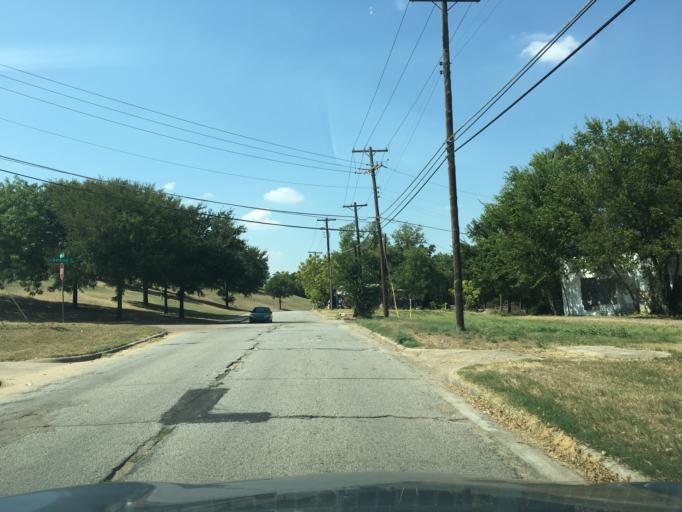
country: US
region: Texas
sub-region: Dallas County
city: Dallas
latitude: 32.7529
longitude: -96.8051
